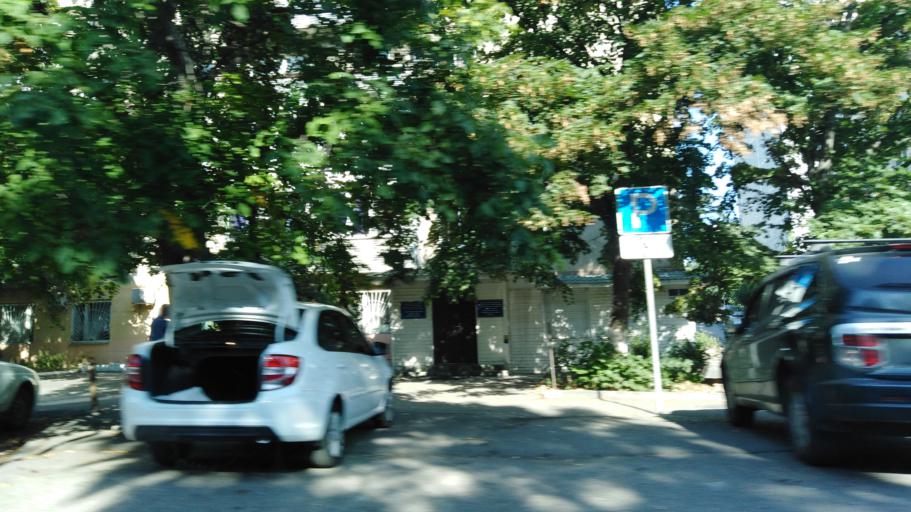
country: RU
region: Stavropol'skiy
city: Pyatigorsk
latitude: 44.0466
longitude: 43.0686
